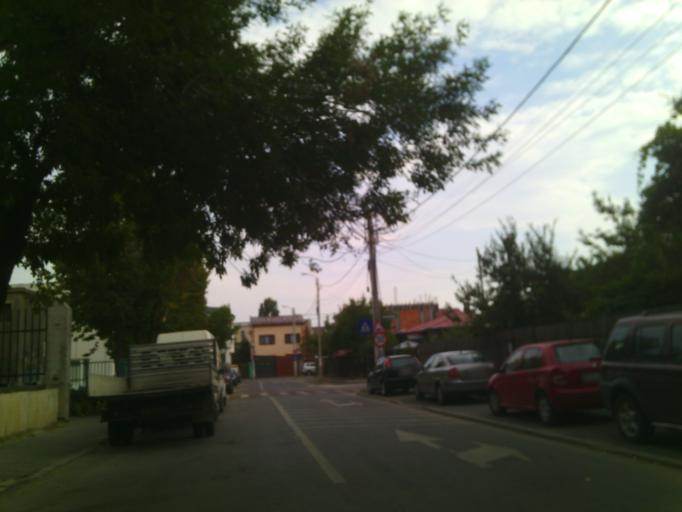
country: RO
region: Bucuresti
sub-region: Municipiul Bucuresti
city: Bucuresti
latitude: 44.3890
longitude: 26.0942
